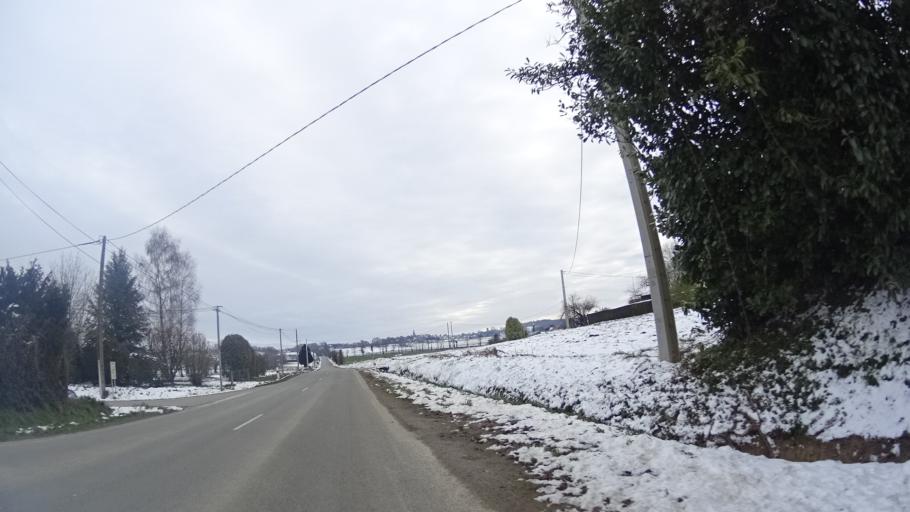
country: FR
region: Brittany
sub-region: Departement des Cotes-d'Armor
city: Plouasne
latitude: 48.3121
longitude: -1.9513
